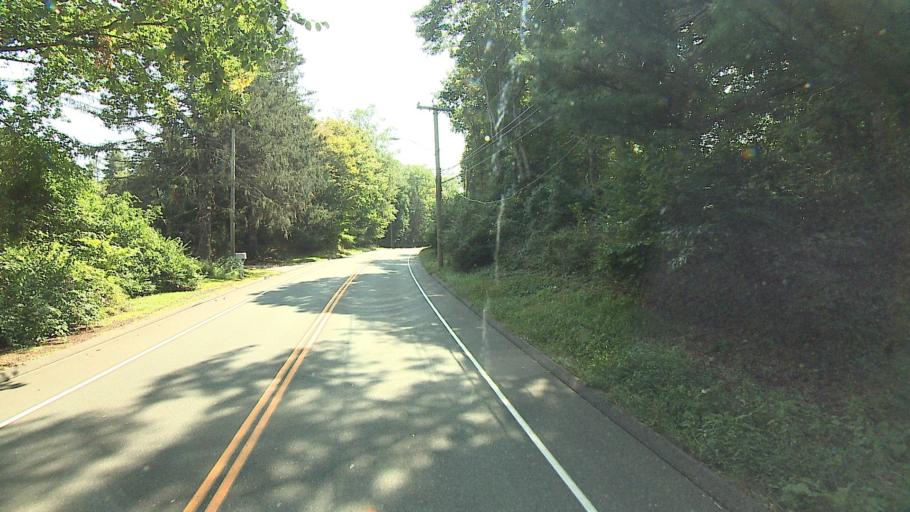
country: US
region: Connecticut
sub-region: Fairfield County
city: Westport
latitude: 41.1732
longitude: -73.3609
